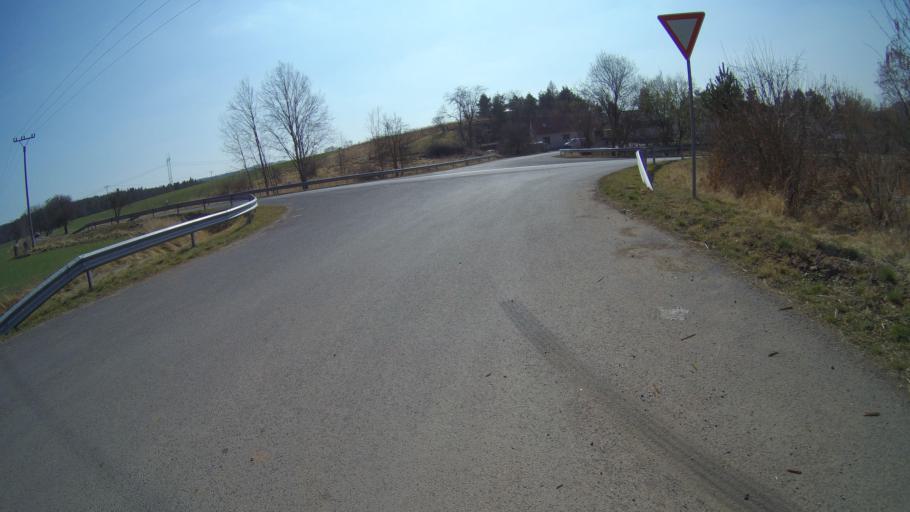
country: CZ
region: Ustecky
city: Mecholupy
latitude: 50.2757
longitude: 13.5703
